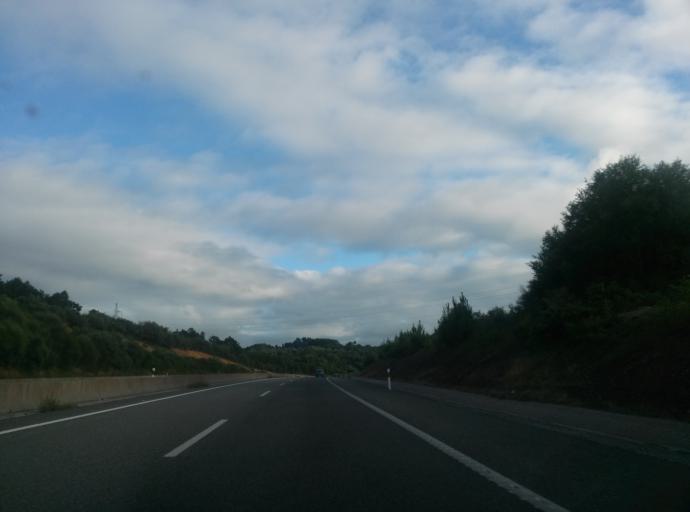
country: ES
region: Galicia
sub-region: Provincia de Lugo
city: Muras
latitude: 43.3823
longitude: -7.7769
